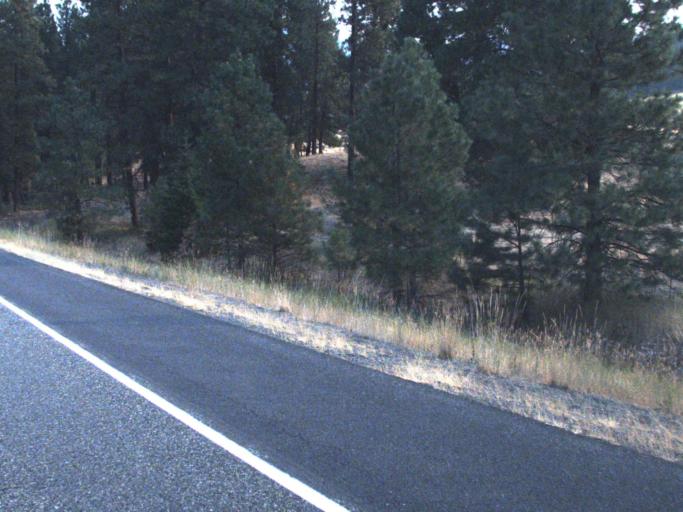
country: US
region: Washington
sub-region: Kittitas County
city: Cle Elum
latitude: 47.1862
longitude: -120.7068
